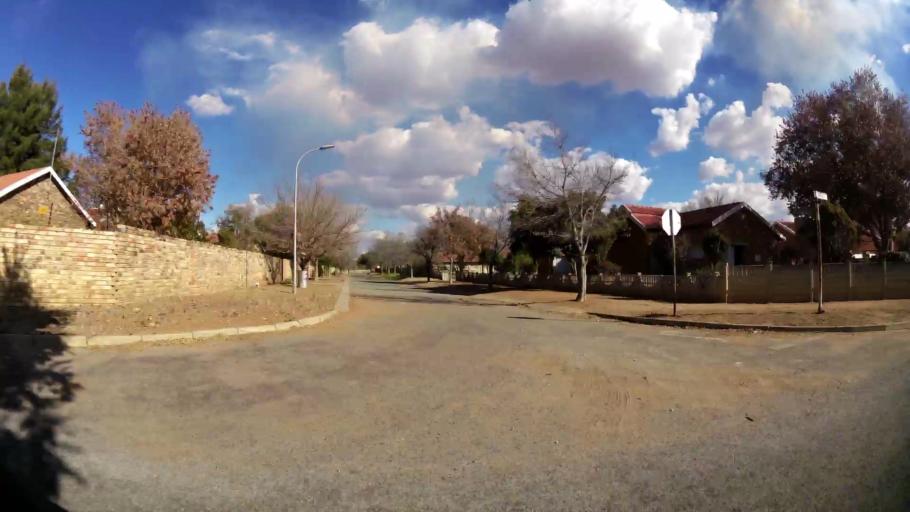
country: ZA
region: North-West
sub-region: Dr Kenneth Kaunda District Municipality
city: Klerksdorp
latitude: -26.8166
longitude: 26.6541
